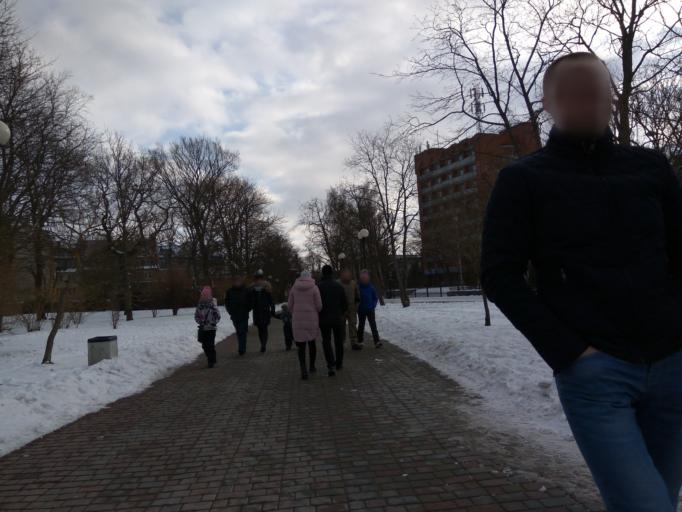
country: RU
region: Kaliningrad
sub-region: Zelenogradskiy Rayon
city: Zelenogradsk
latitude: 54.9614
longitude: 20.4755
